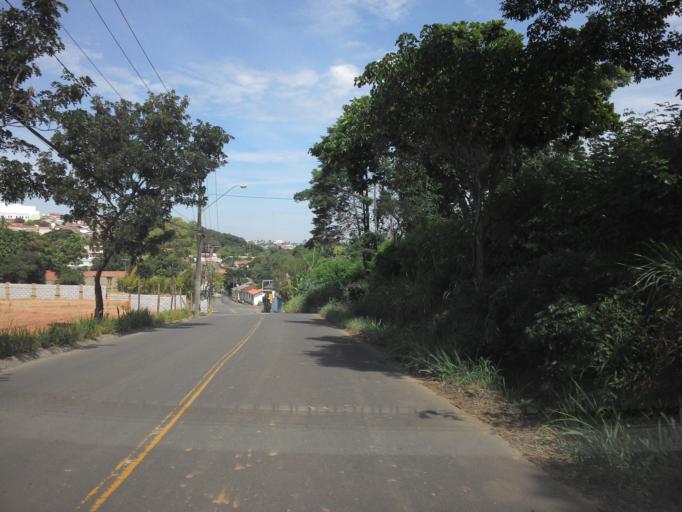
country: BR
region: Sao Paulo
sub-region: Valinhos
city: Valinhos
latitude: -22.9430
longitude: -46.9829
